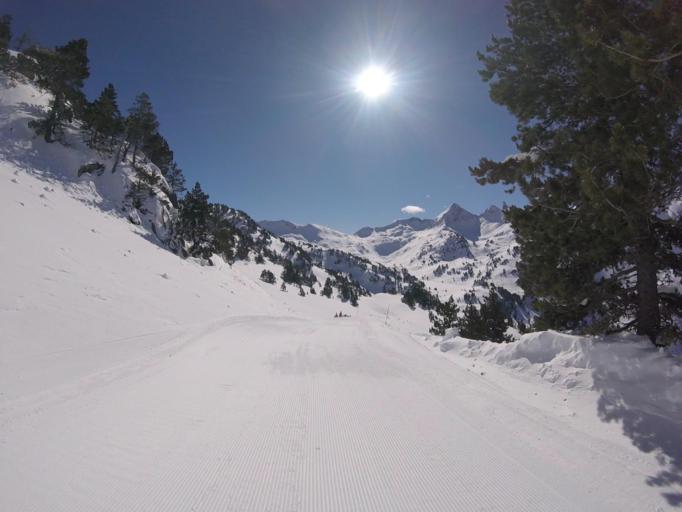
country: ES
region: Catalonia
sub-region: Provincia de Lleida
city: Espot
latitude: 42.7052
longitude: 0.9769
